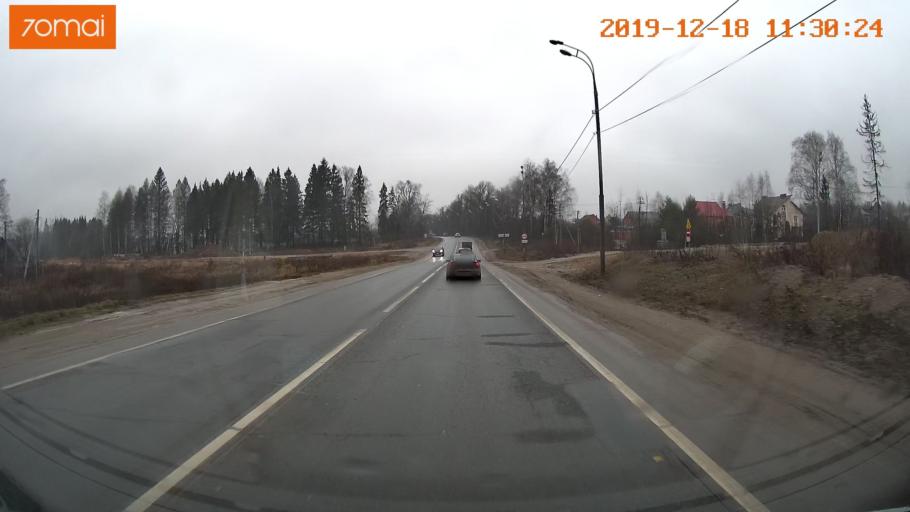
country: RU
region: Moskovskaya
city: Bol'shiye Vyazemy
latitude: 55.6571
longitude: 36.9684
